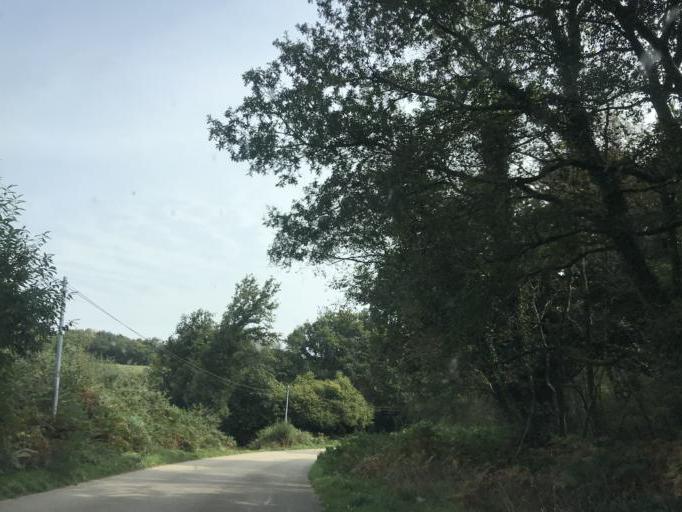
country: FR
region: Brittany
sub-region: Departement du Finistere
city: Brasparts
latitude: 48.3267
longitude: -3.9250
